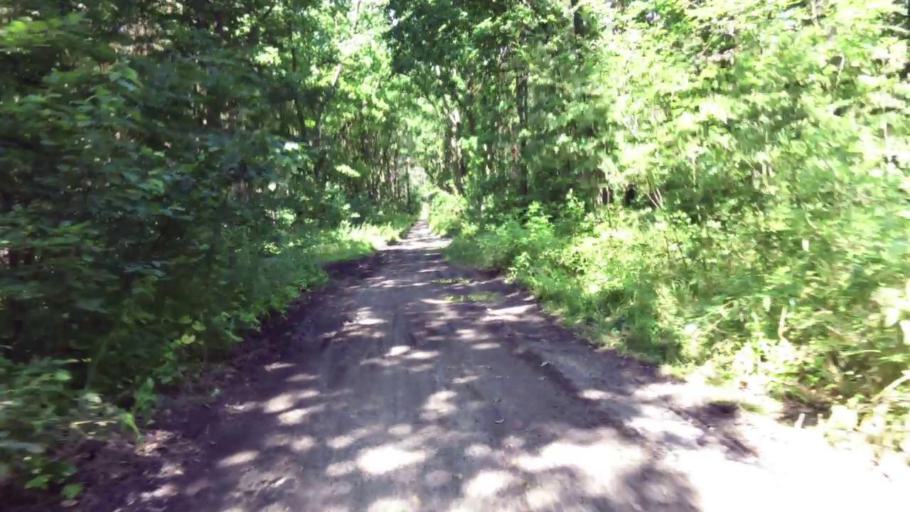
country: PL
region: West Pomeranian Voivodeship
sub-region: Powiat gryfinski
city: Stare Czarnowo
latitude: 53.3481
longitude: 14.7624
